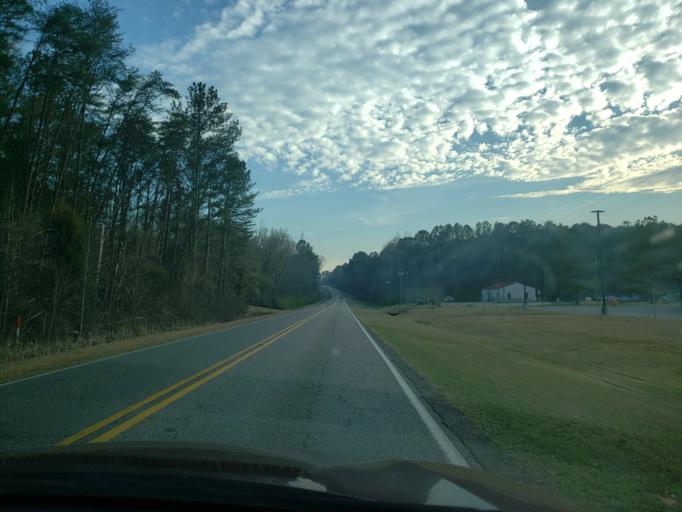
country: US
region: Alabama
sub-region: Hale County
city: Greensboro
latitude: 32.7228
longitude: -87.5917
